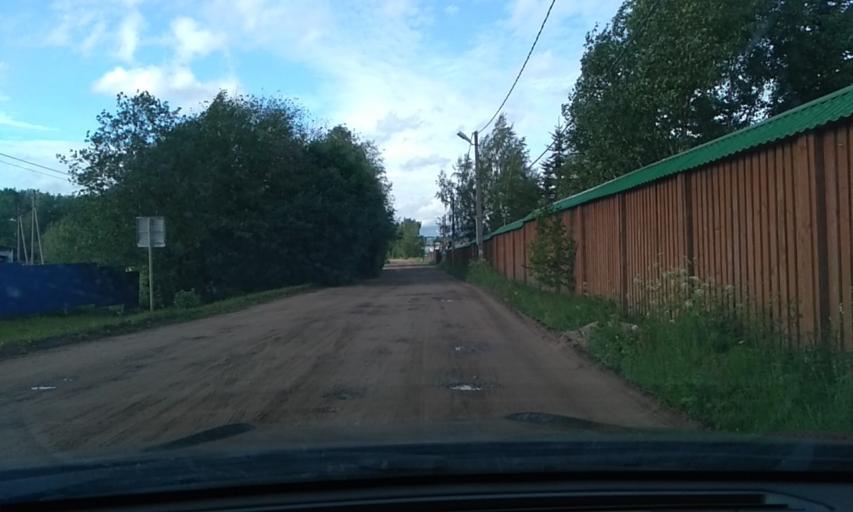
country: RU
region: Leningrad
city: Otradnoye
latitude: 59.7988
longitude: 30.8007
